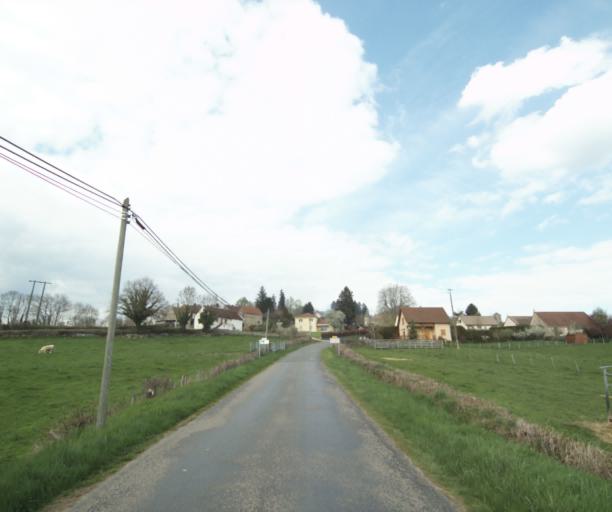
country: FR
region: Bourgogne
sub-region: Departement de Saone-et-Loire
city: Ciry-le-Noble
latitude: 46.5268
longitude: 4.3308
